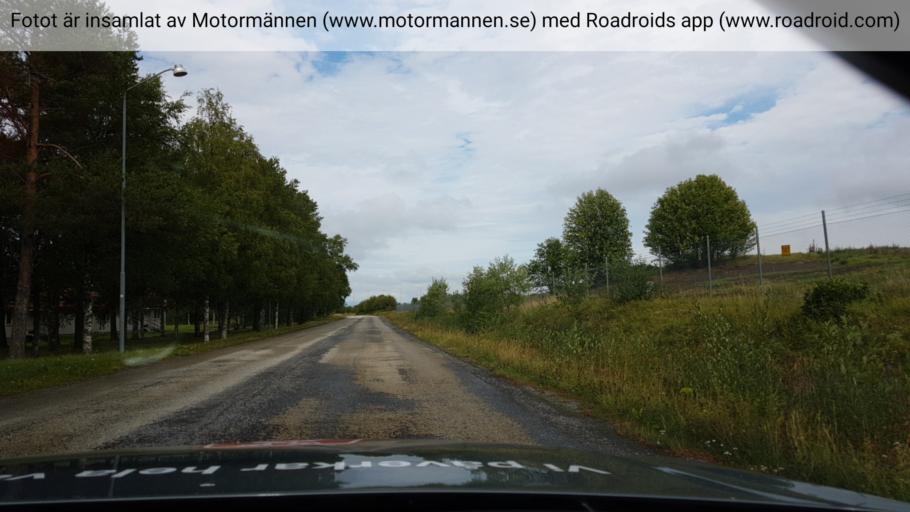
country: SE
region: Jaemtland
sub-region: Krokoms Kommun
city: Krokom
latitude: 63.1975
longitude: 14.4761
